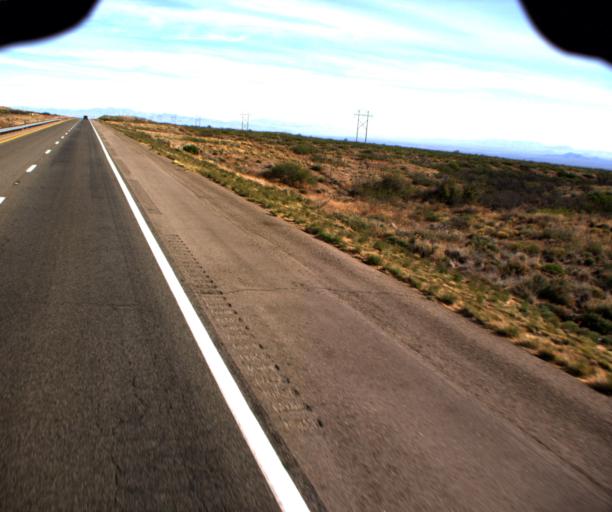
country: US
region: Arizona
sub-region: Graham County
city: Swift Trail Junction
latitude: 32.4973
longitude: -109.6736
